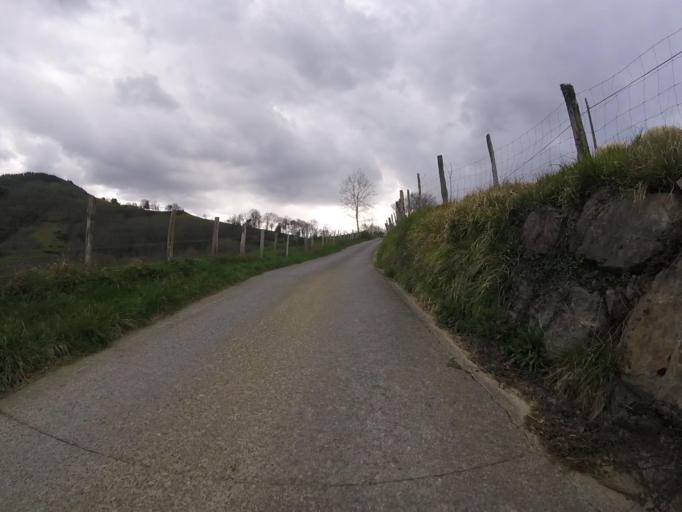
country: ES
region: Basque Country
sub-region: Provincia de Guipuzcoa
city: Errenteria
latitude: 43.2815
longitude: -1.8596
